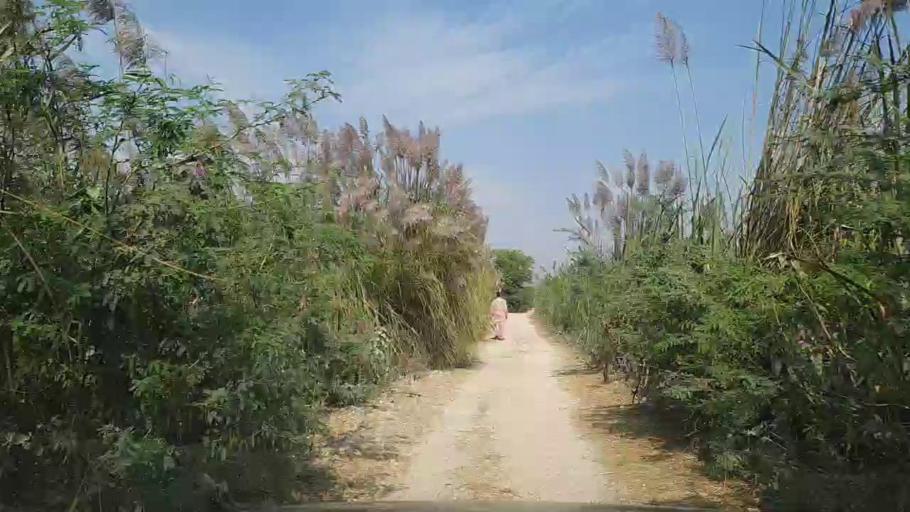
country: PK
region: Sindh
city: Thatta
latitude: 24.7596
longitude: 67.7655
